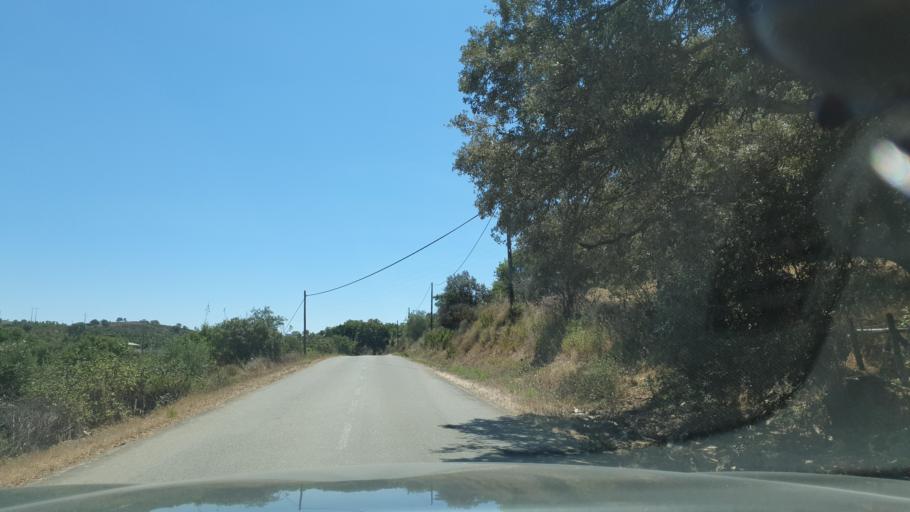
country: PT
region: Beja
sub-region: Odemira
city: Odemira
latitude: 37.5514
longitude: -8.4272
